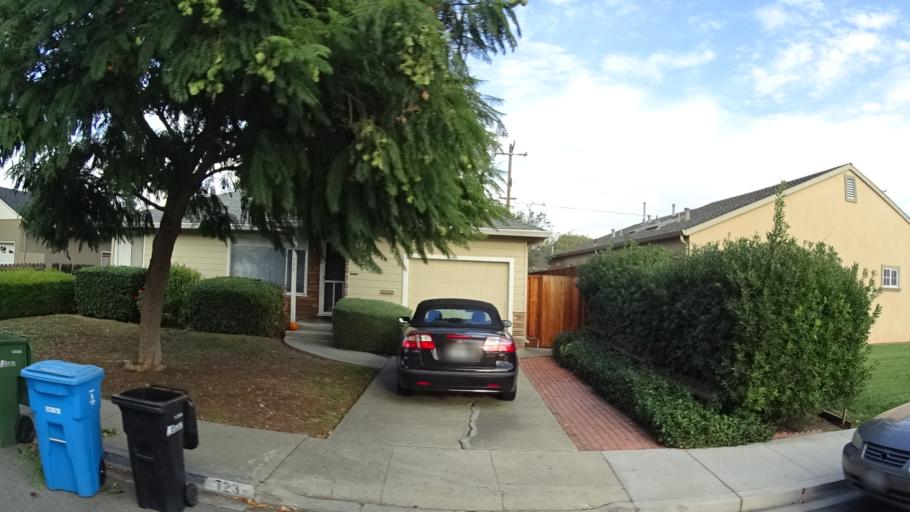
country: US
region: California
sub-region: Santa Clara County
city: Santa Clara
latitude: 37.3405
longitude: -121.9622
